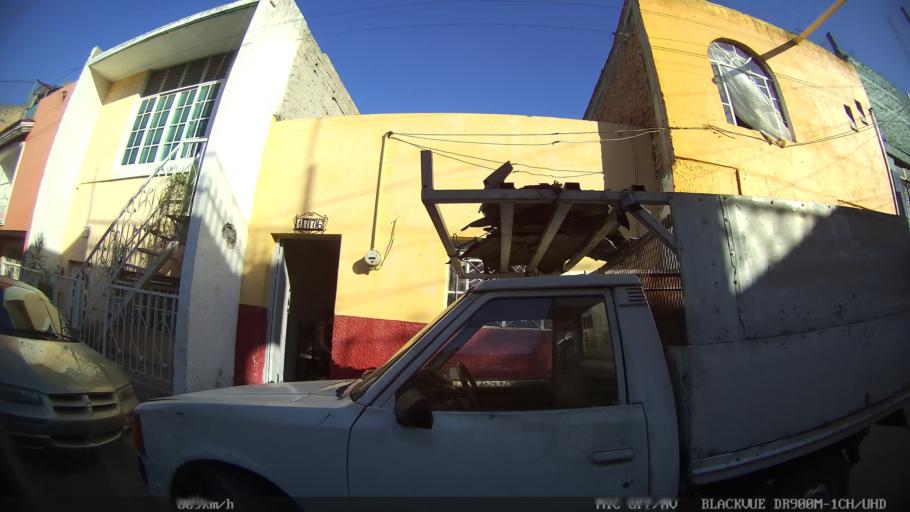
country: MX
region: Jalisco
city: Tlaquepaque
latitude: 20.7044
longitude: -103.2944
